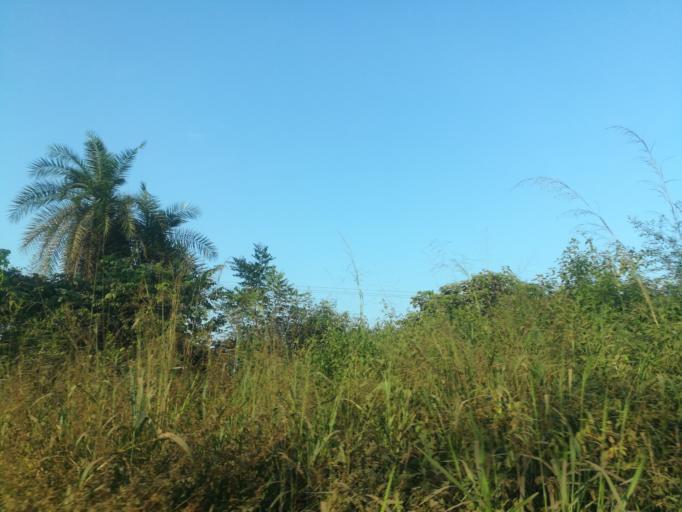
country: NG
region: Ogun
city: Abeokuta
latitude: 7.2101
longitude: 3.2012
